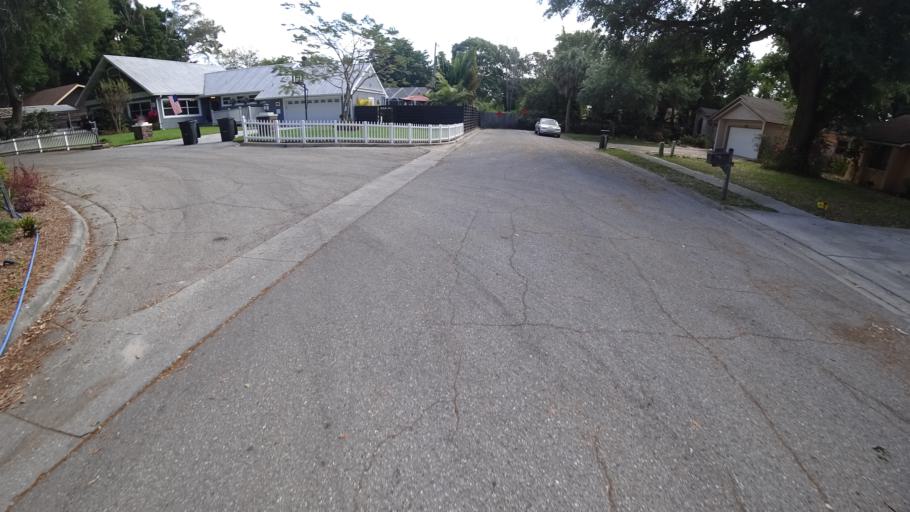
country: US
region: Florida
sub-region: Manatee County
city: Whitfield
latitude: 27.4194
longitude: -82.5687
